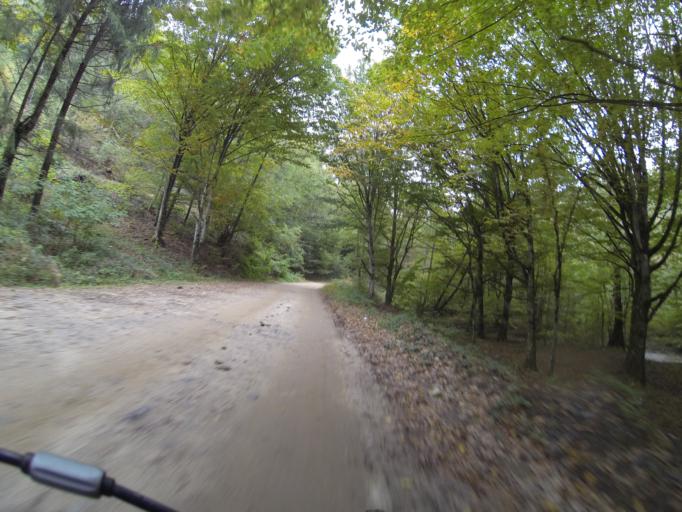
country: RO
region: Gorj
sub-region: Comuna Tismana
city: Pocruia
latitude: 45.0559
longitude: 22.9064
